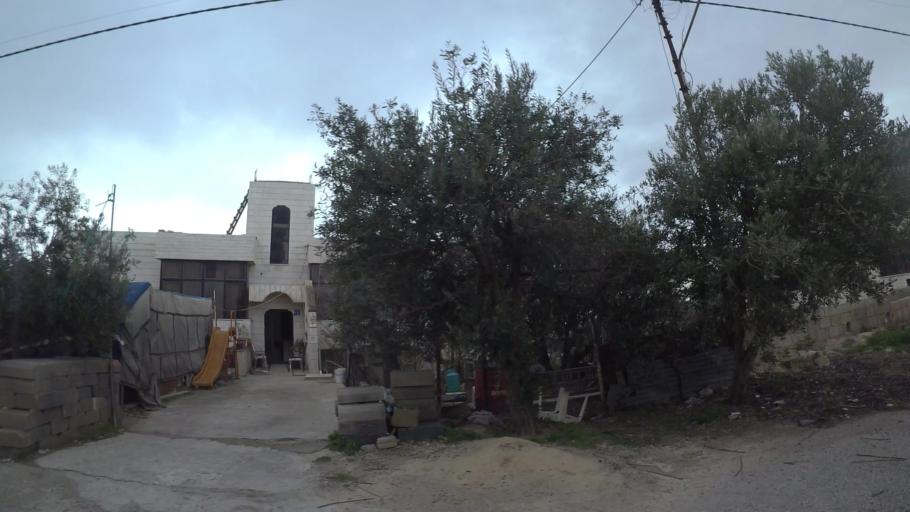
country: JO
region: Amman
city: Umm as Summaq
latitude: 31.9059
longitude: 35.8332
